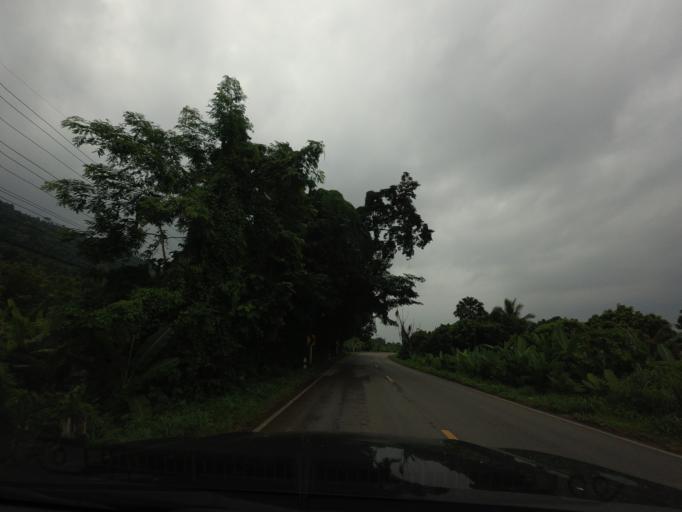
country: TH
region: Nong Khai
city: Sangkhom
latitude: 18.0448
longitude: 102.3333
